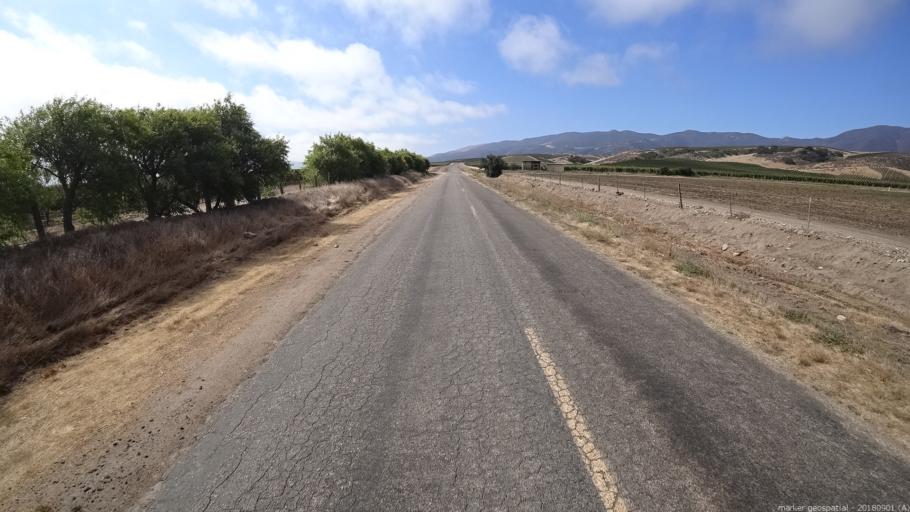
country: US
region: California
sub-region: Monterey County
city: Soledad
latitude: 36.3602
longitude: -121.3355
